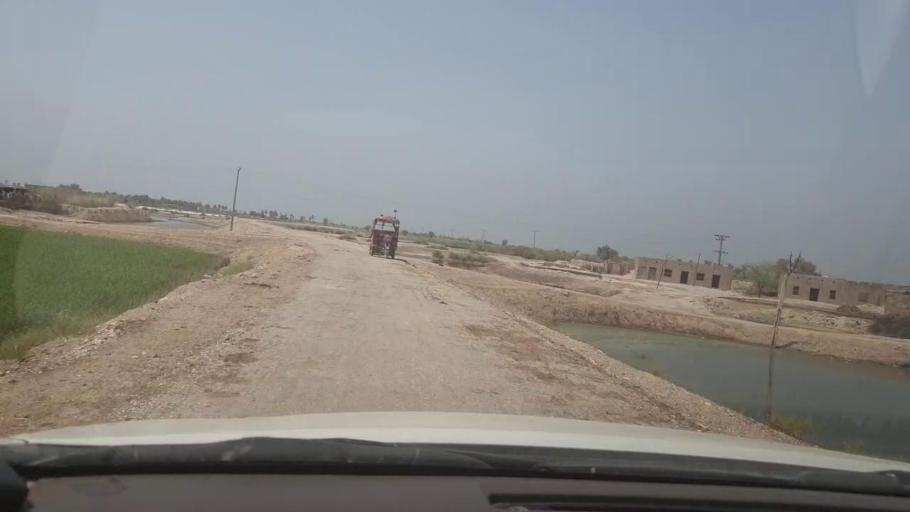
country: PK
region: Sindh
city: Garhi Yasin
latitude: 27.9719
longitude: 68.5495
